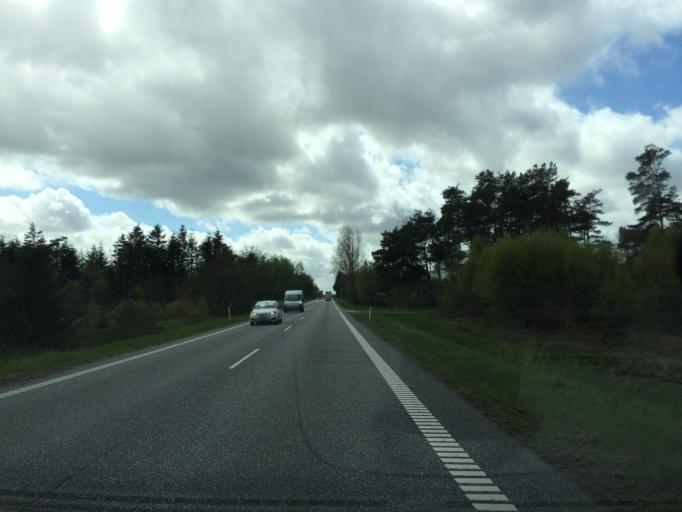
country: DK
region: Central Jutland
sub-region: Viborg Kommune
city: Stoholm
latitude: 56.4157
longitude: 9.0295
